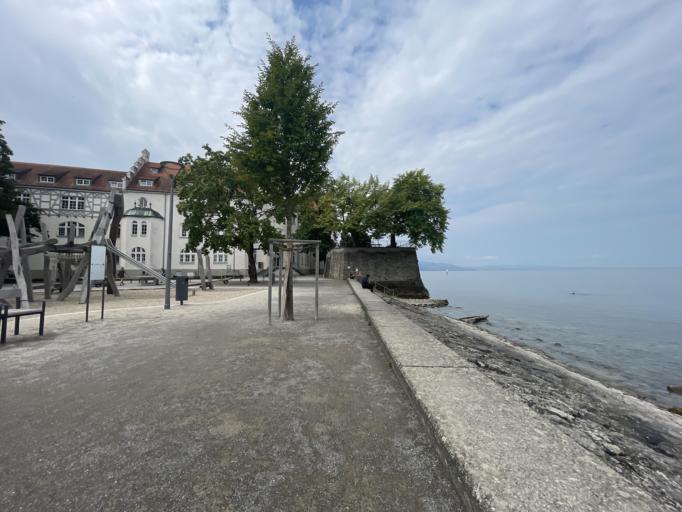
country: DE
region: Bavaria
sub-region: Swabia
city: Lindau
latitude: 47.5466
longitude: 9.6763
